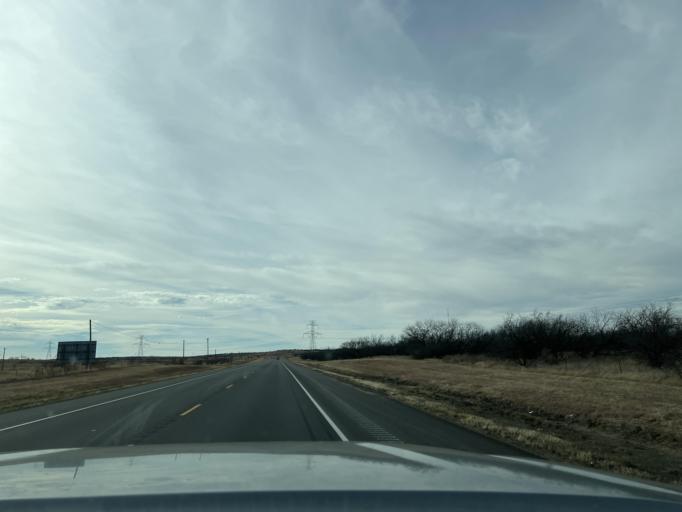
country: US
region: Texas
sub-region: Shackelford County
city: Albany
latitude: 32.7055
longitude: -99.3989
